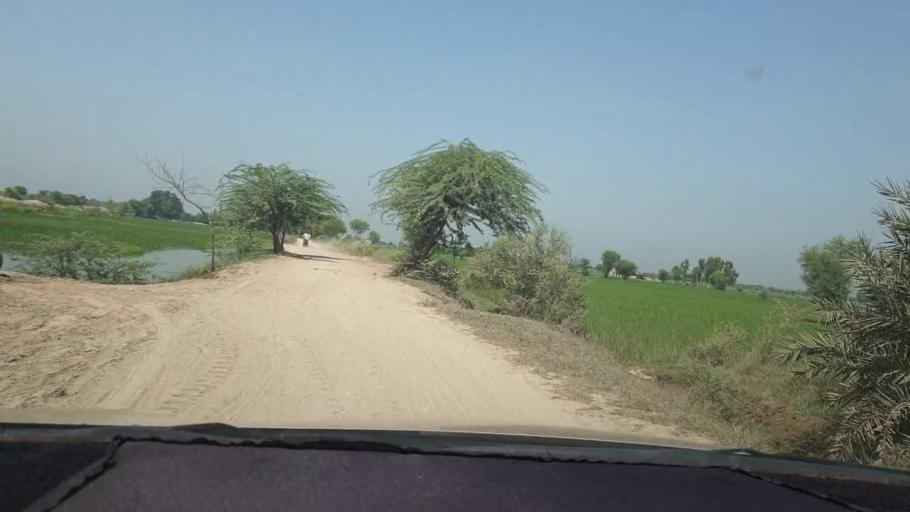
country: PK
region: Sindh
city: Kambar
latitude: 27.6102
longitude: 68.0655
